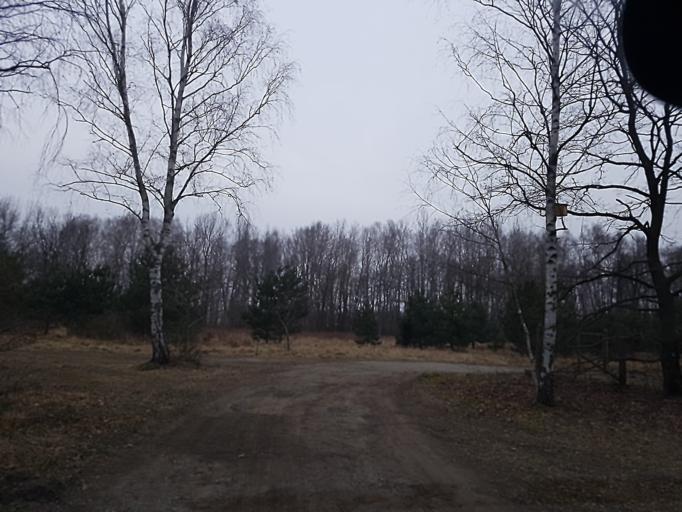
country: DE
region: Brandenburg
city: Ruckersdorf
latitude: 51.5953
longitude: 13.5595
